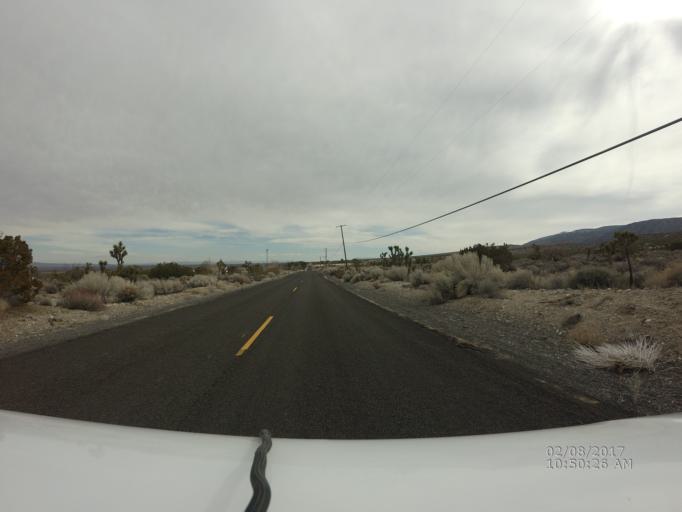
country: US
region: California
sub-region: San Bernardino County
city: Pinon Hills
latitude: 34.4695
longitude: -117.7583
